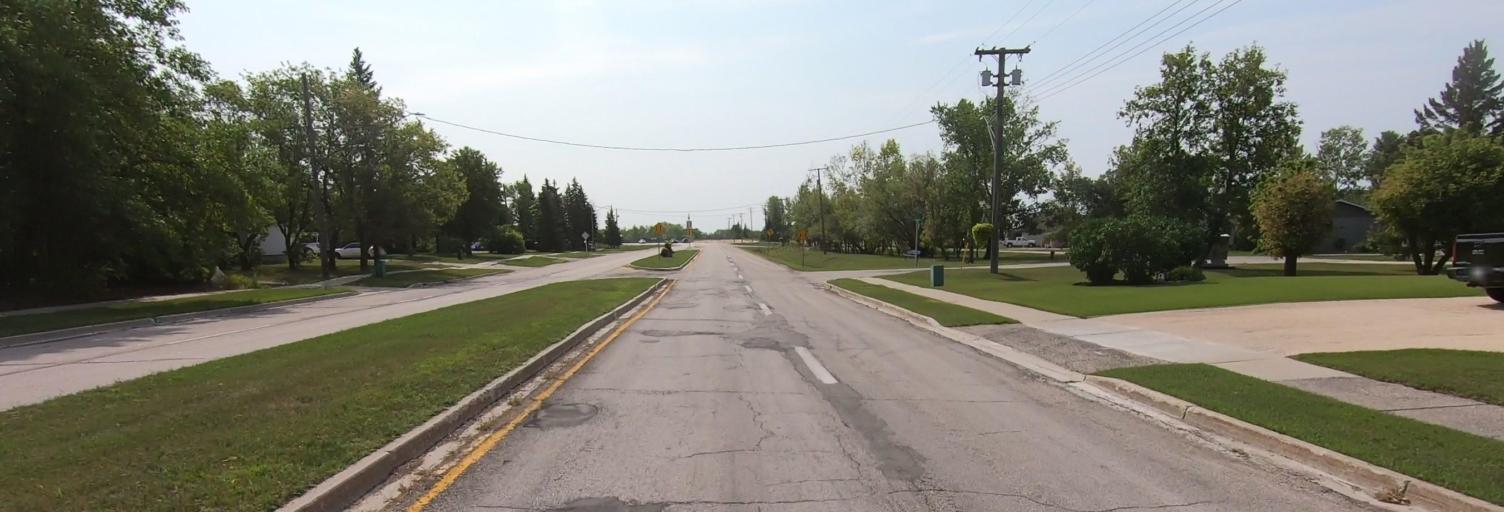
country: CA
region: Manitoba
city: Niverville
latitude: 49.6690
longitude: -97.1124
